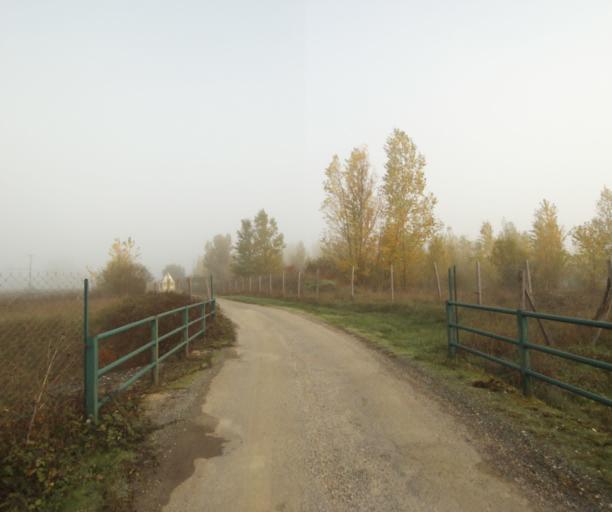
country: FR
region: Midi-Pyrenees
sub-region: Departement du Tarn-et-Garonne
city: Nohic
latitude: 43.8967
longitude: 1.4590
